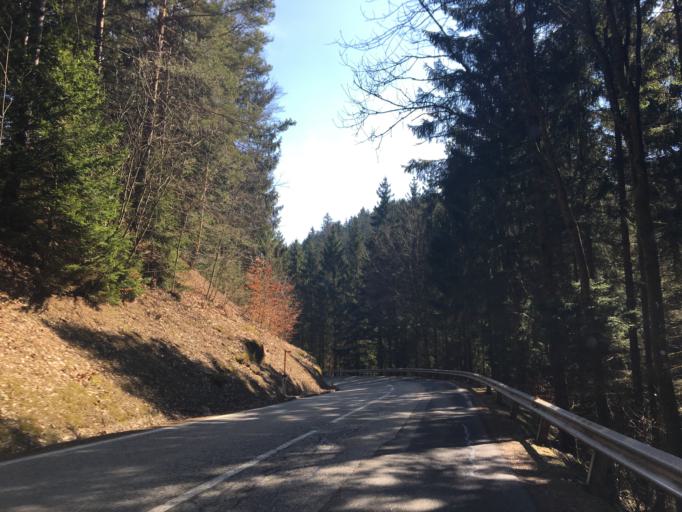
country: AT
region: Upper Austria
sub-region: Politischer Bezirk Perg
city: Sankt Georgen am Walde
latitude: 48.2808
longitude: 14.9070
